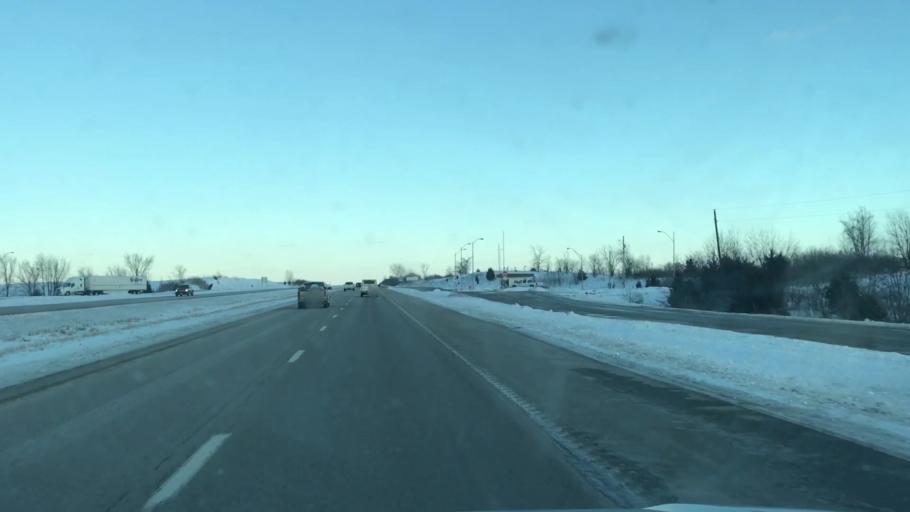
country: US
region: Missouri
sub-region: Andrew County
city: Country Club Village
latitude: 39.7476
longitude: -94.6970
